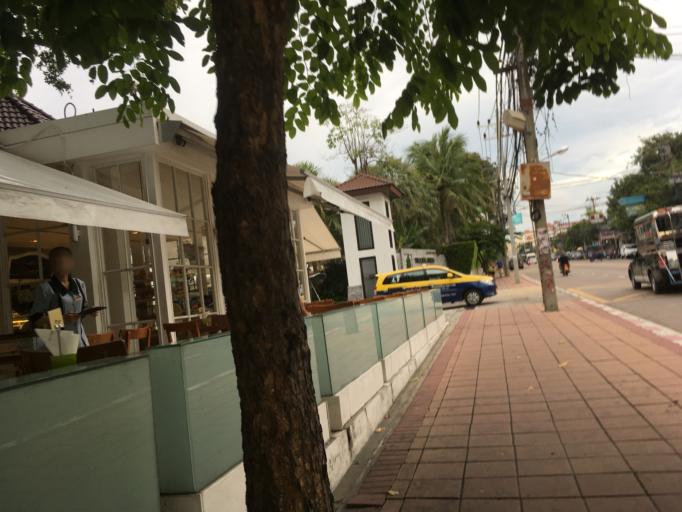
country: TH
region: Chon Buri
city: Phatthaya
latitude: 12.9519
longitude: 100.8881
